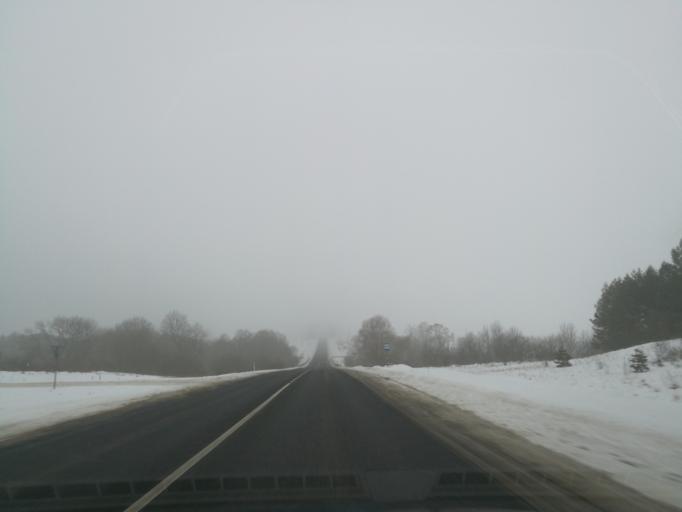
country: LT
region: Utenos apskritis
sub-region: Anyksciai
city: Anyksciai
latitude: 55.5157
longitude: 25.0516
